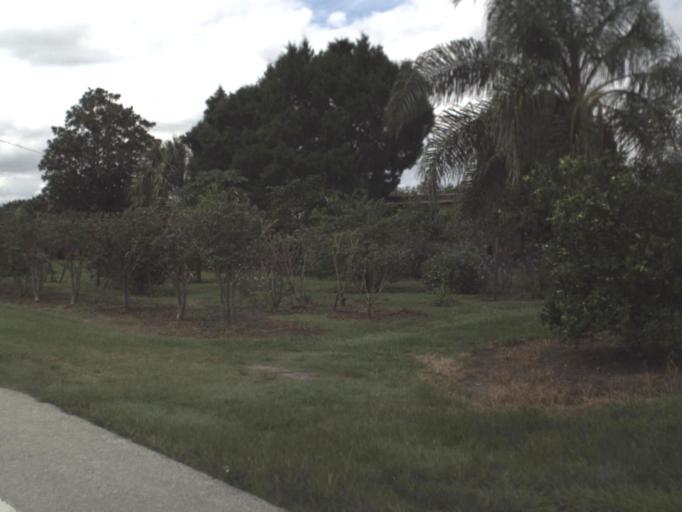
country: US
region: Florida
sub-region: Hardee County
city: Bowling Green
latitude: 27.5948
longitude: -81.9552
